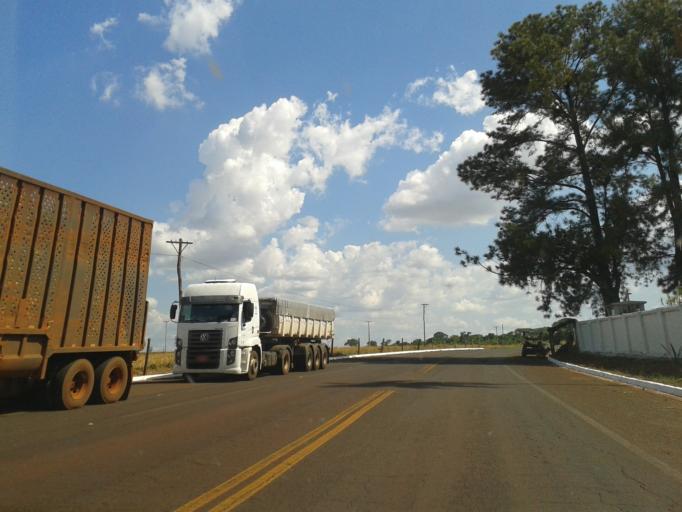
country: BR
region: Minas Gerais
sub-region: Centralina
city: Centralina
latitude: -18.7389
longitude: -49.2055
